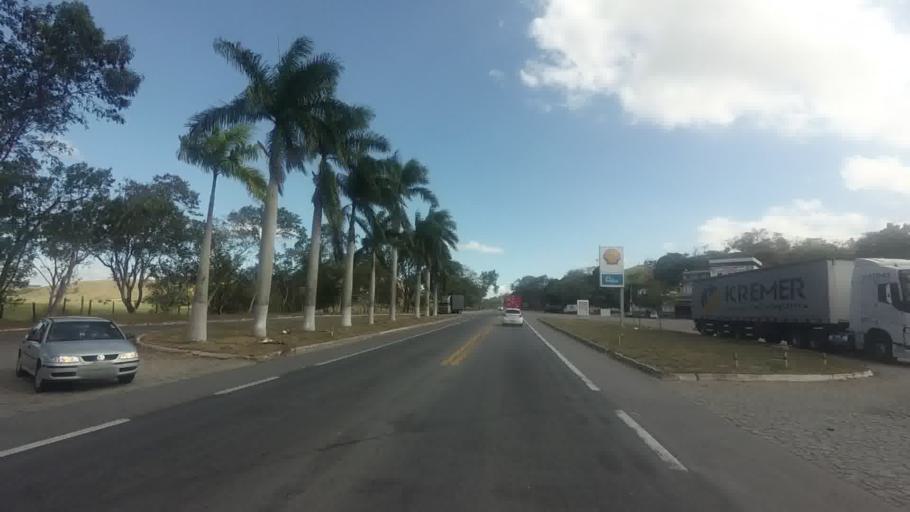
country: BR
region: Espirito Santo
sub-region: Viana
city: Viana
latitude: -20.4093
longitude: -40.4586
